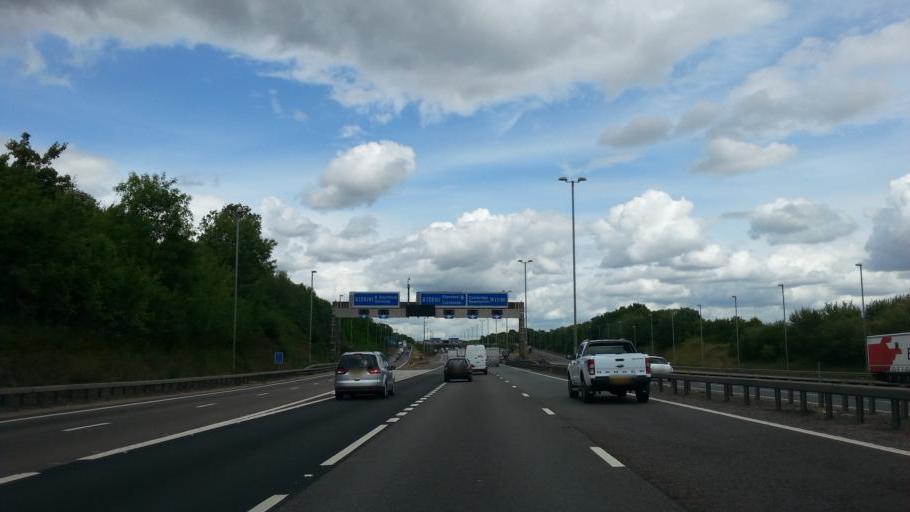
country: GB
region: England
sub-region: Essex
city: Little Hallingbury
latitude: 51.8654
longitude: 0.1944
